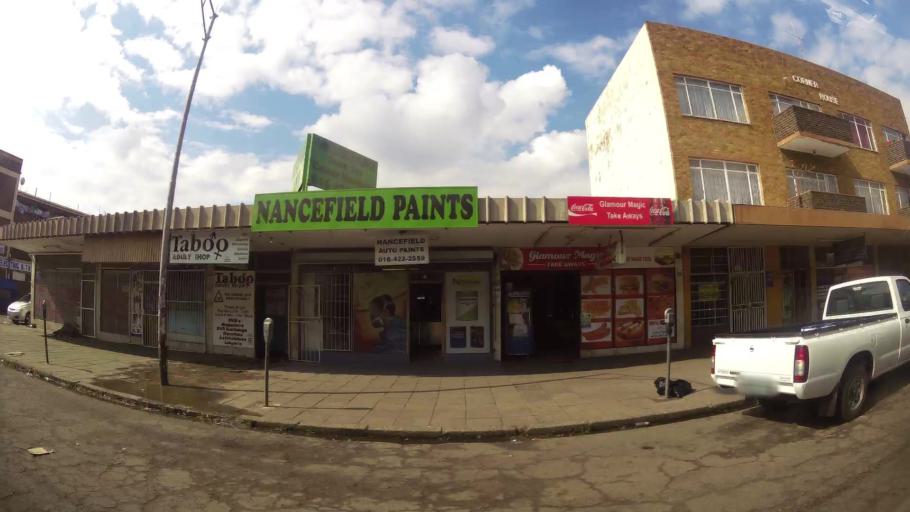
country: ZA
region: Gauteng
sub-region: Sedibeng District Municipality
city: Vereeniging
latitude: -26.6715
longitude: 27.9302
